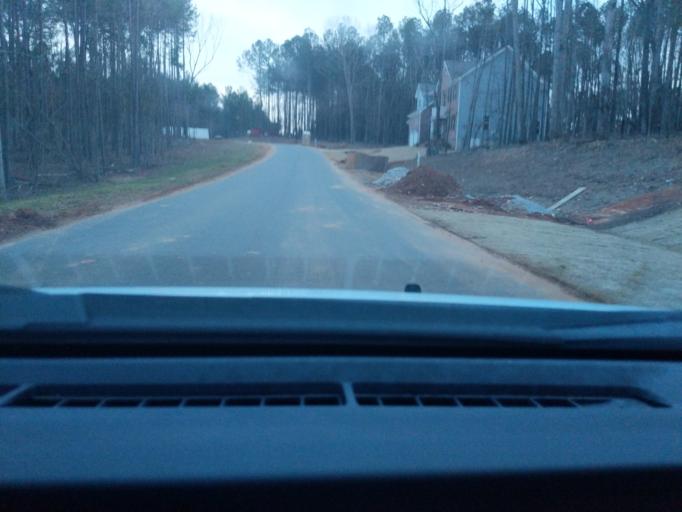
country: US
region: North Carolina
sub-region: Wake County
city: Garner
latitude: 35.7111
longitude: -78.6837
